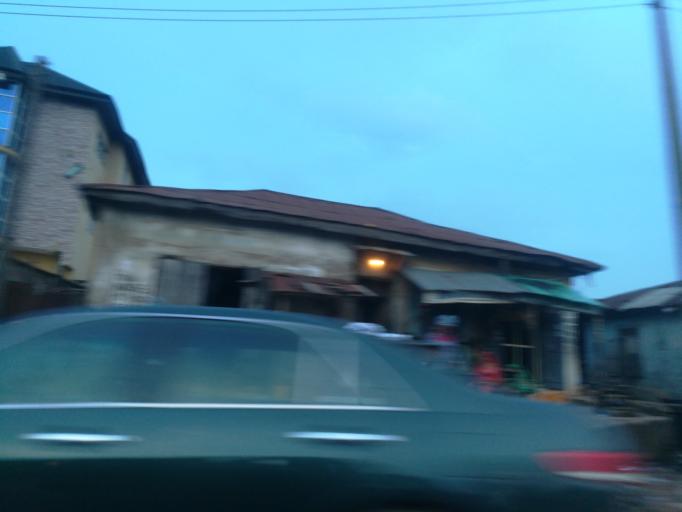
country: NG
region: Oyo
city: Ibadan
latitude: 7.3877
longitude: 3.9007
